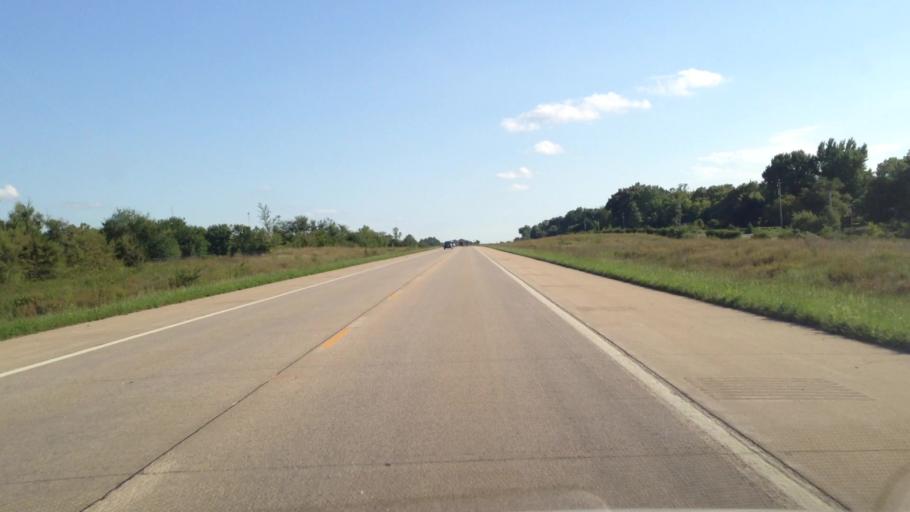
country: US
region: Kansas
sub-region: Crawford County
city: Arma
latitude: 37.5676
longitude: -94.7047
